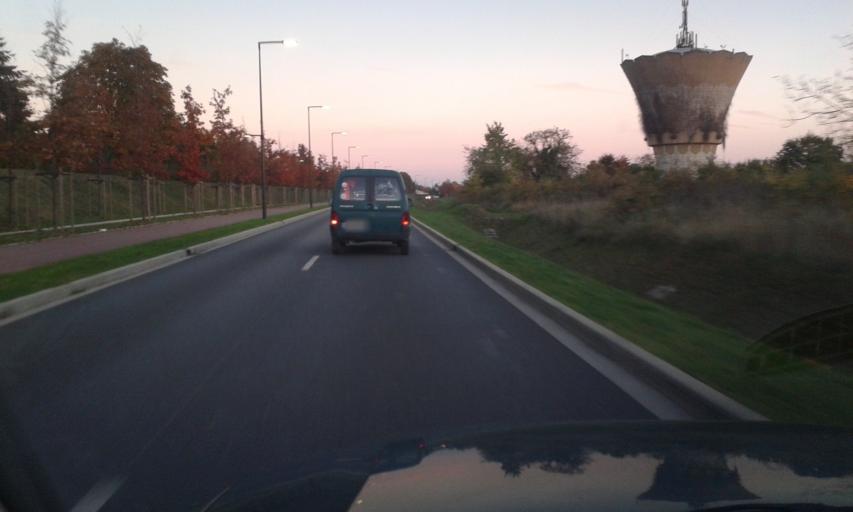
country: FR
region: Centre
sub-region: Departement du Loiret
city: Olivet
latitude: 47.8585
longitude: 1.8898
